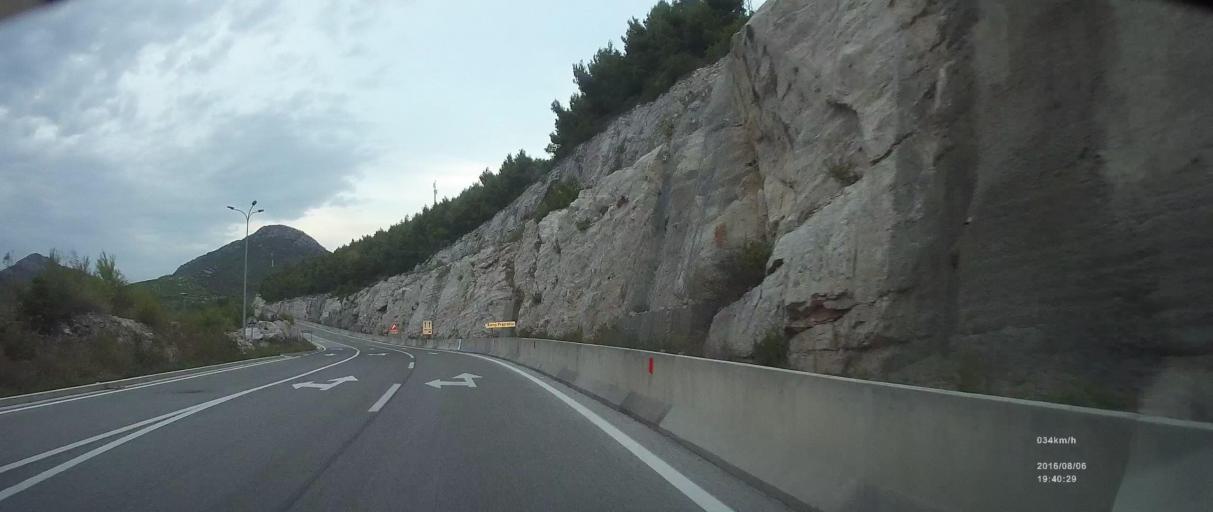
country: HR
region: Dubrovacko-Neretvanska
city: Ston
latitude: 42.8140
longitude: 17.6796
